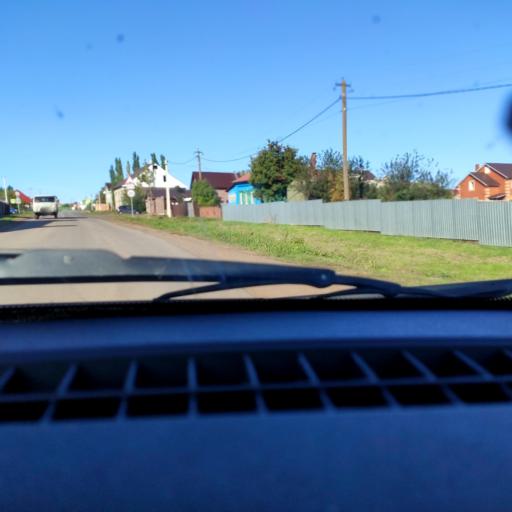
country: RU
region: Bashkortostan
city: Avdon
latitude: 54.6058
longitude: 55.7923
